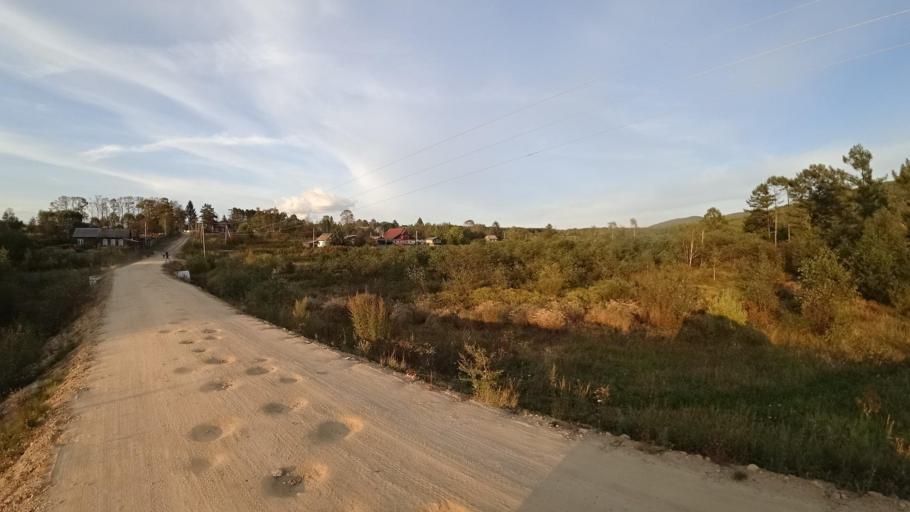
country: RU
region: Jewish Autonomous Oblast
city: Kul'dur
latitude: 49.2058
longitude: 131.6400
